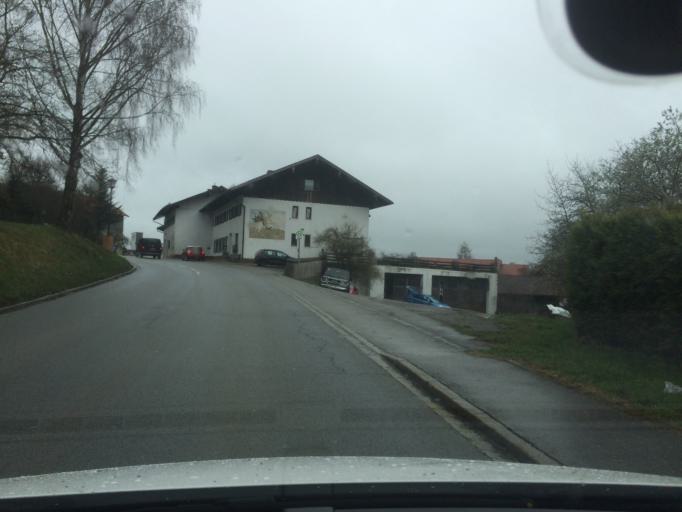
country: DE
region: Bavaria
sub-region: Upper Bavaria
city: Assling
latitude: 47.9775
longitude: 11.9555
